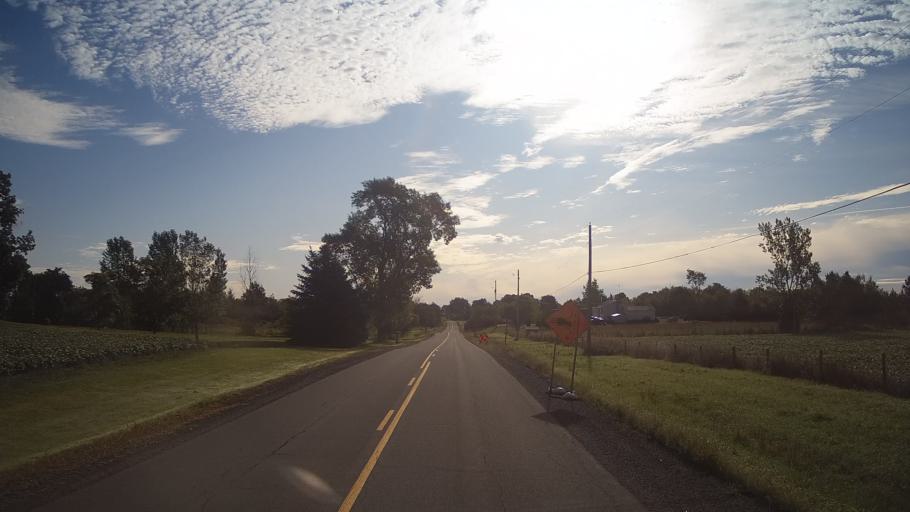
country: CA
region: Ontario
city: Gananoque
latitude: 44.4001
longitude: -76.1034
